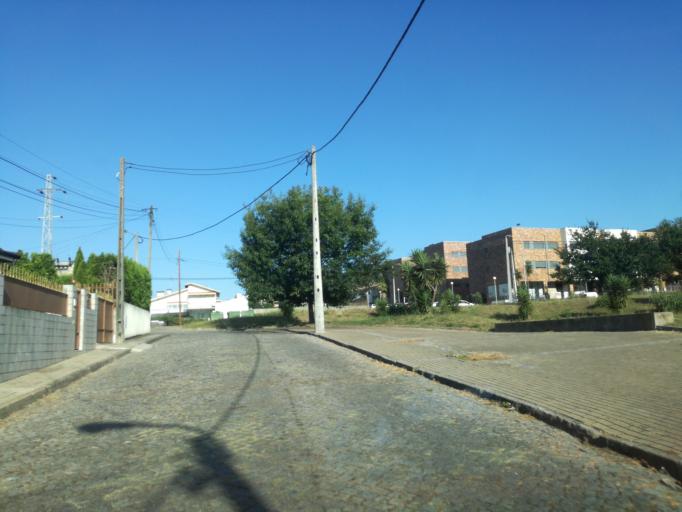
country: PT
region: Porto
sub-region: Trofa
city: Sao Romao do Coronado
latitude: 41.2631
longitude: -8.5709
